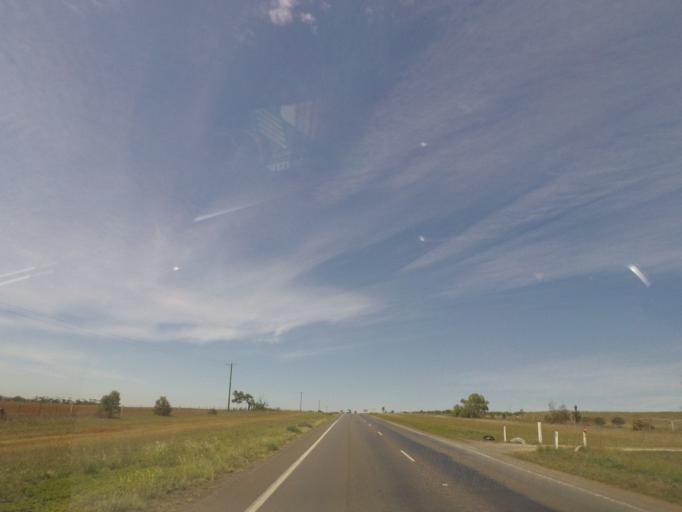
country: AU
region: Victoria
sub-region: Moorabool
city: Bacchus Marsh
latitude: -37.7697
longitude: 144.4394
